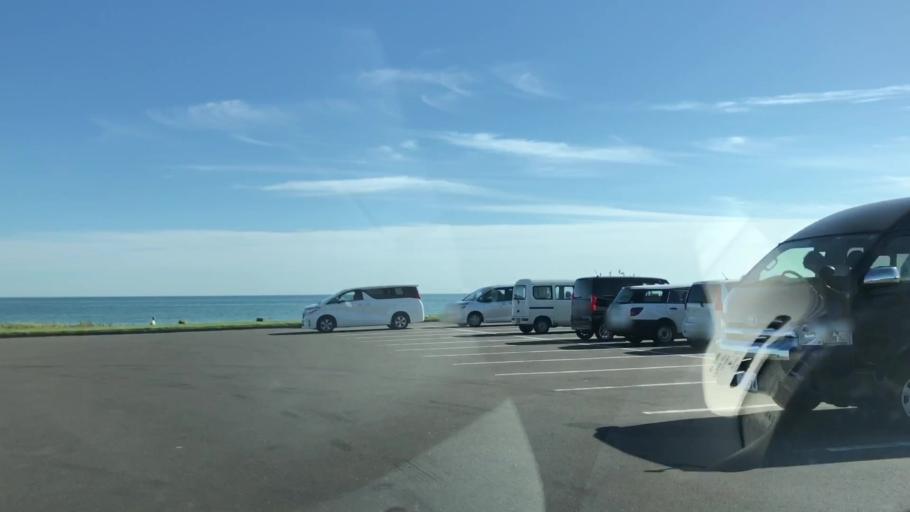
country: JP
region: Hokkaido
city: Kushiro
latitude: 42.9930
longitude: 144.1990
